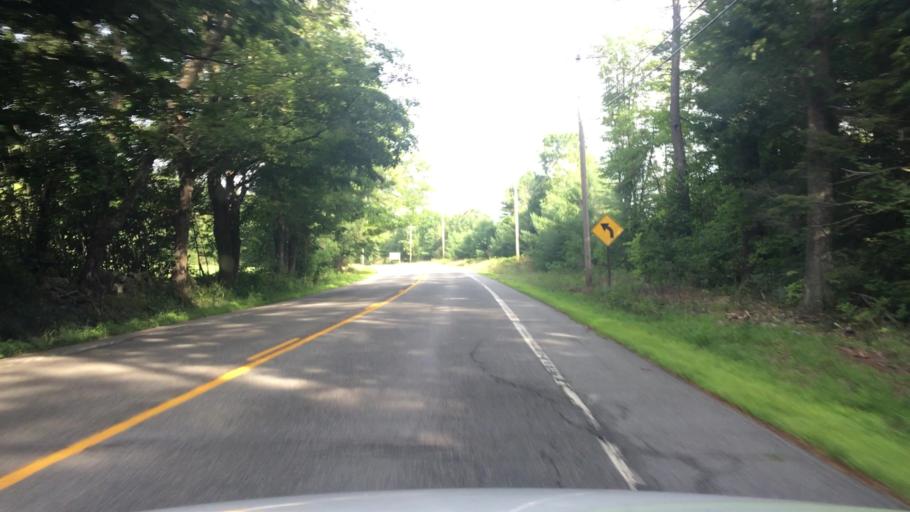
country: US
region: Maine
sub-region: York County
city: Cornish
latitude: 43.8042
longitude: -70.8328
